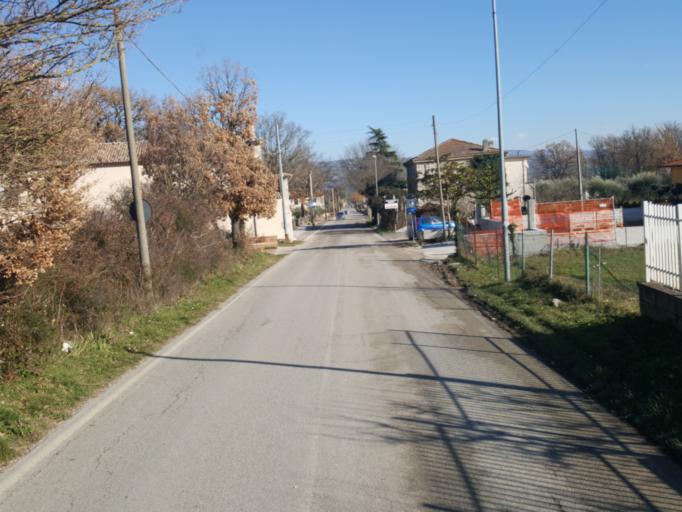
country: IT
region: Campania
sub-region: Provincia di Benevento
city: Morcone
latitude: 41.3427
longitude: 14.6790
